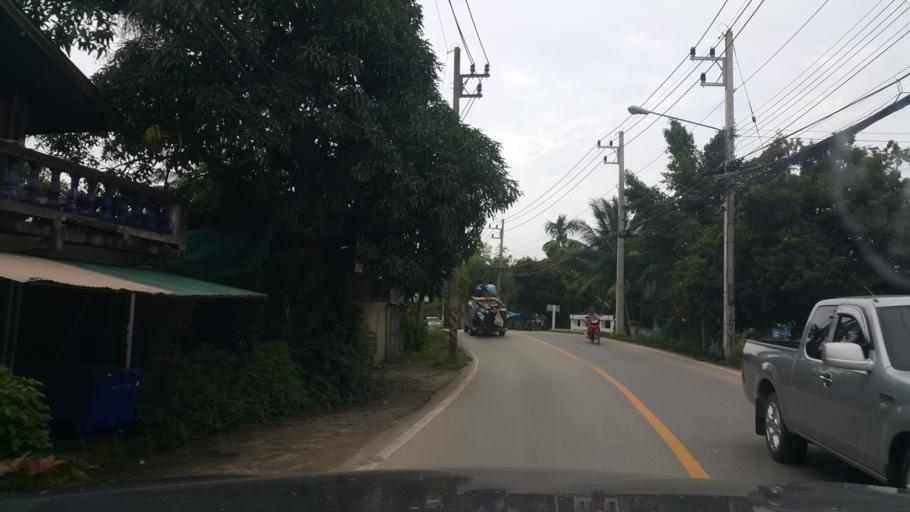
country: TH
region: Chiang Mai
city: San Sai
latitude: 18.8577
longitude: 99.0507
